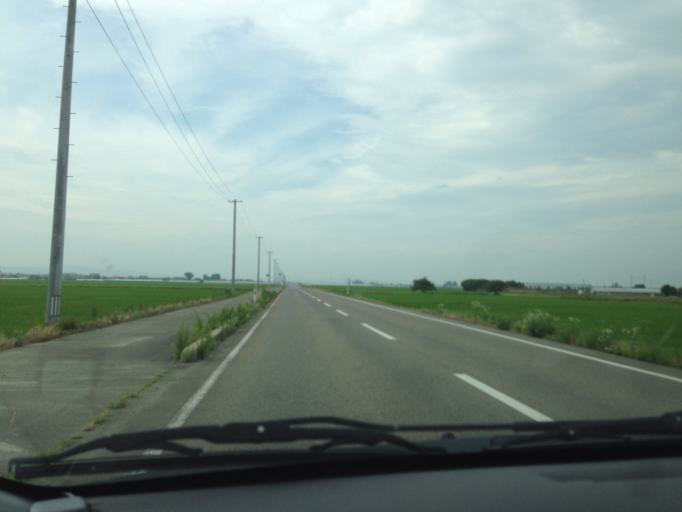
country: JP
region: Fukushima
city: Kitakata
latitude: 37.4941
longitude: 139.8551
